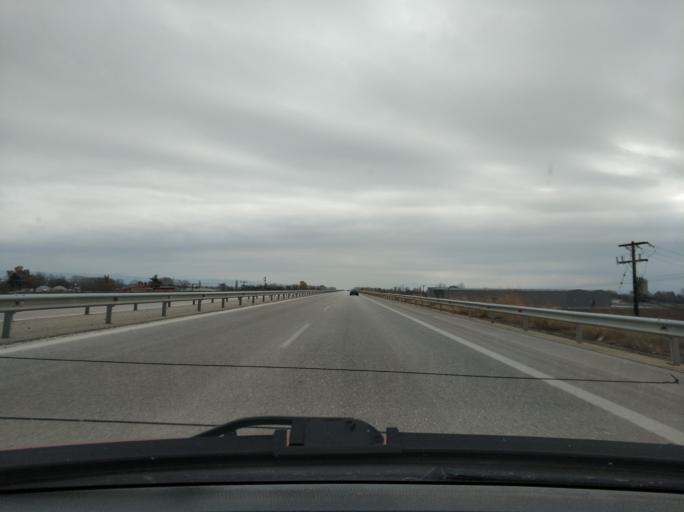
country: GR
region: Central Macedonia
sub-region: Nomos Thessalonikis
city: Kavallari
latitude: 40.7354
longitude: 23.0367
